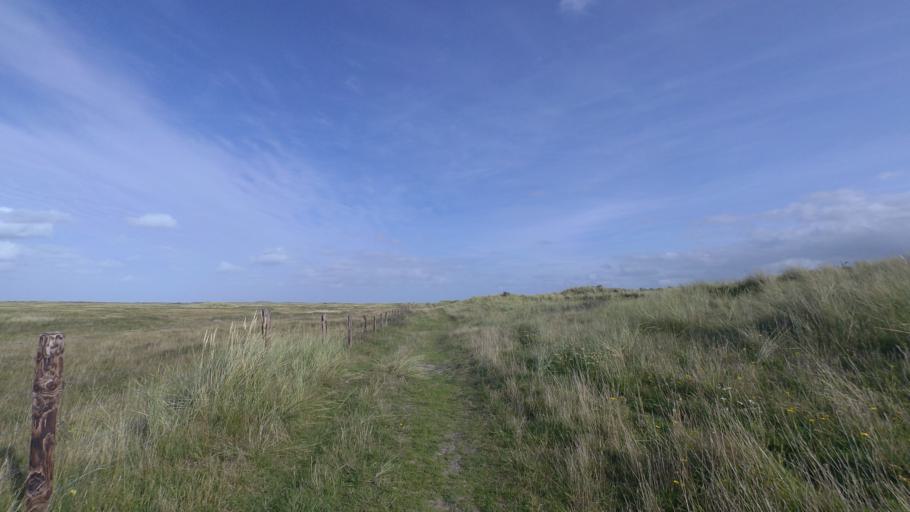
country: NL
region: Friesland
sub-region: Gemeente Ameland
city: Nes
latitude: 53.4527
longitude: 5.8466
